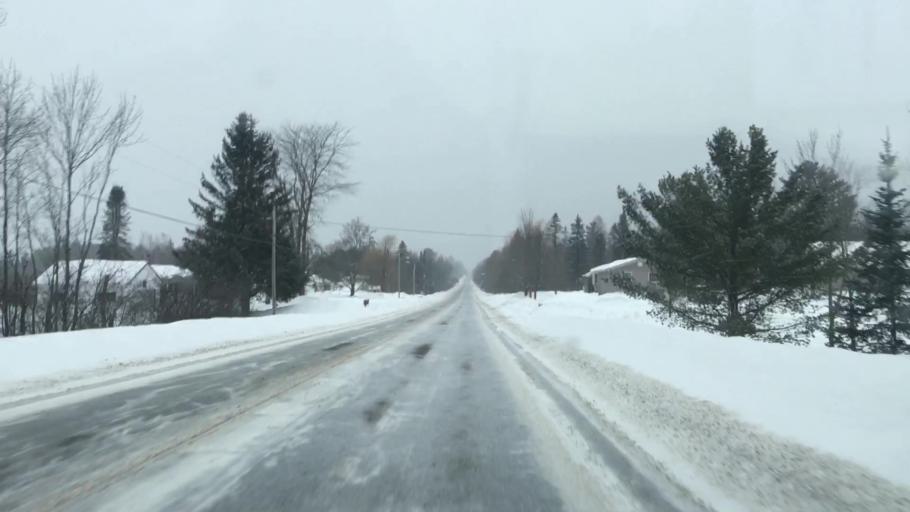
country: US
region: Maine
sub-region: Penobscot County
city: Medway
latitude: 45.5248
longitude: -68.3566
